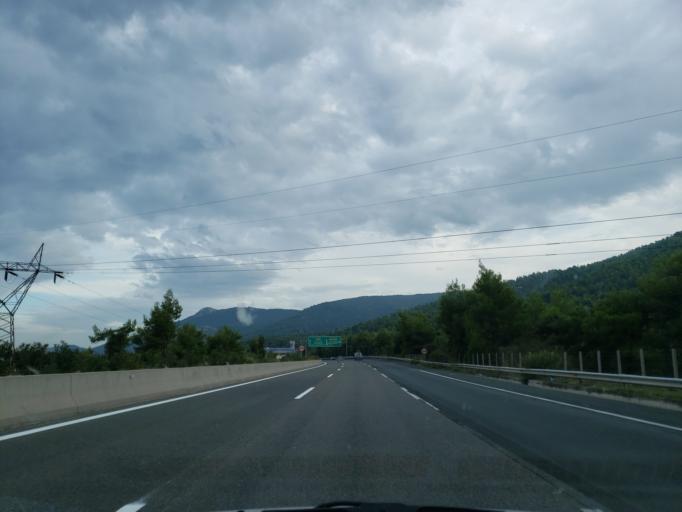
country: GR
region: Attica
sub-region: Nomarchia Anatolikis Attikis
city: Oropos
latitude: 38.2419
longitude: 23.7724
